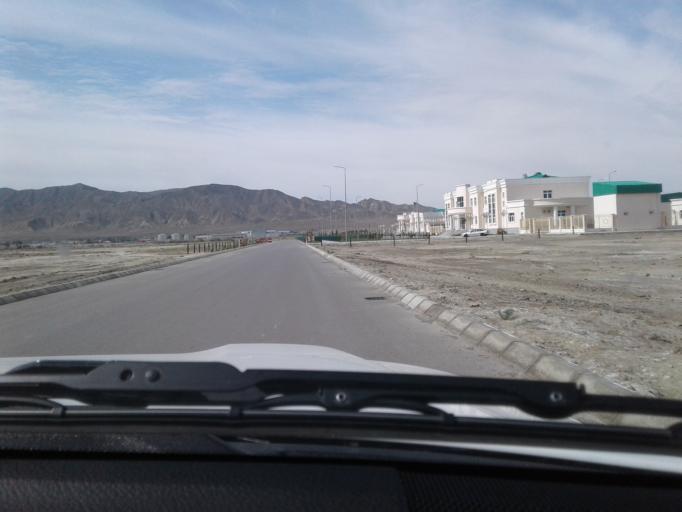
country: TM
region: Balkan
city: Gazanjyk
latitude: 39.2650
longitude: 55.4908
